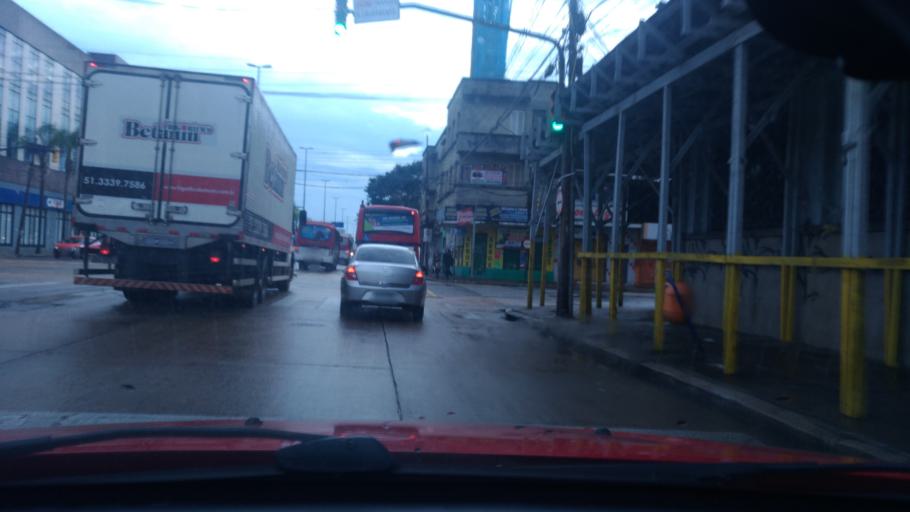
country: BR
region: Rio Grande do Sul
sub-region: Porto Alegre
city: Porto Alegre
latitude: -30.0107
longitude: -51.2026
